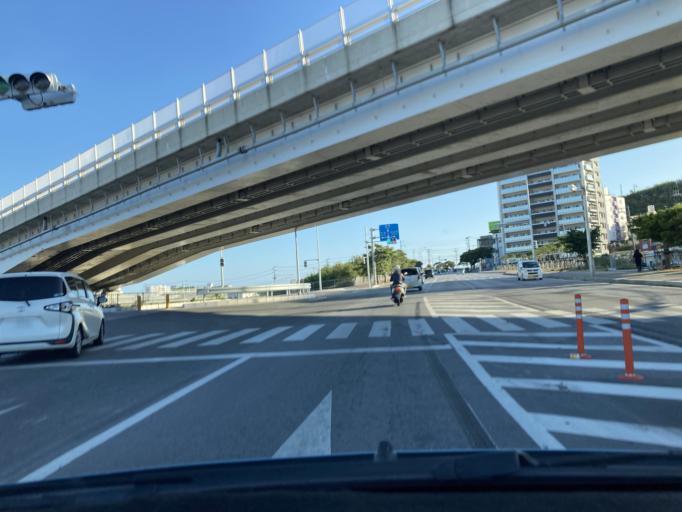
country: JP
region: Okinawa
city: Ginowan
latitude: 26.2423
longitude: 127.7401
